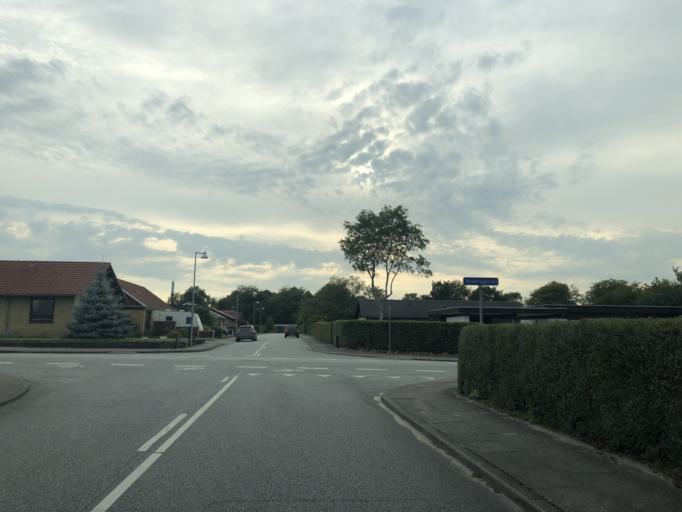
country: DK
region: Central Jutland
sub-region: Herning Kommune
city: Herning
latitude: 56.1477
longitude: 8.9515
